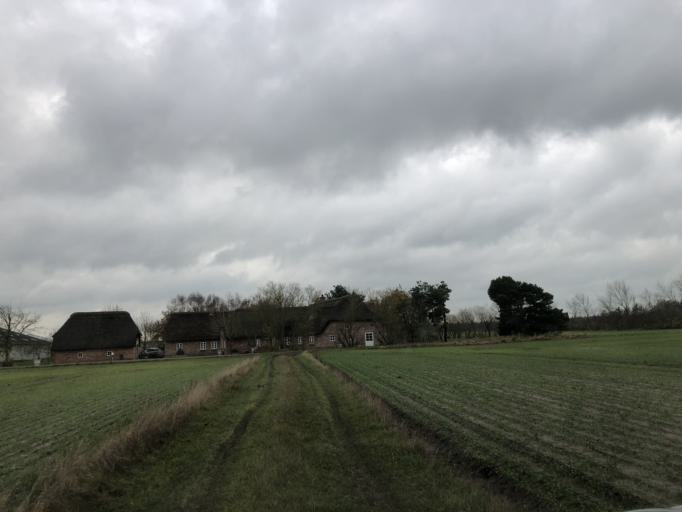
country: DK
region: Central Jutland
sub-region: Holstebro Kommune
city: Ulfborg
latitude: 56.3122
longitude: 8.2048
